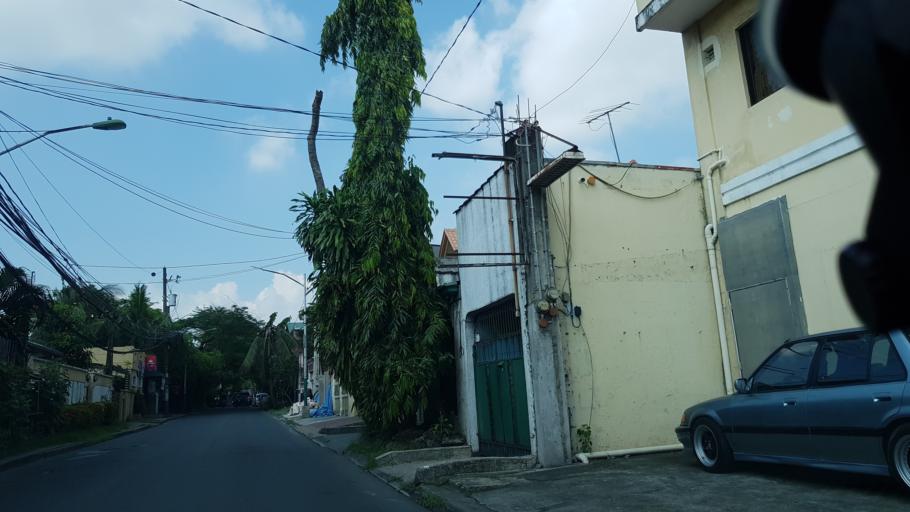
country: PH
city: Sambayanihan People's Village
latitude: 14.4761
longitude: 121.0275
